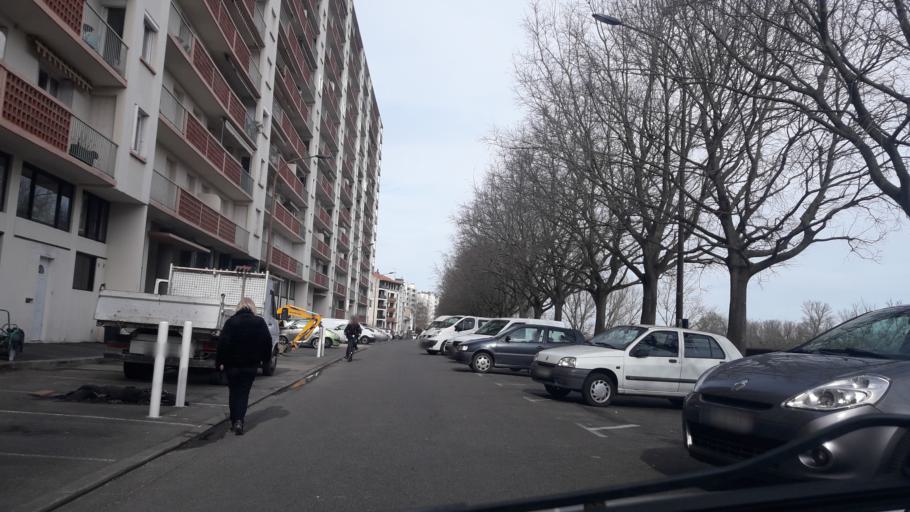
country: FR
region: Midi-Pyrenees
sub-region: Departement de la Haute-Garonne
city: Toulouse
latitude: 43.5822
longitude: 1.4279
